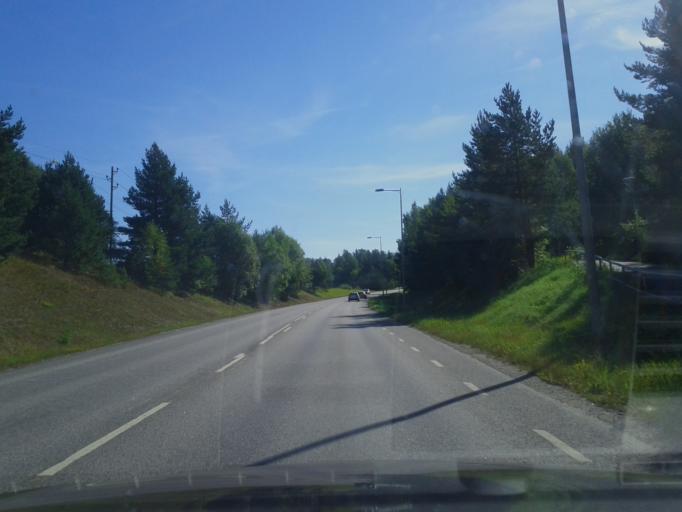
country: SE
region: Stockholm
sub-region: Taby Kommun
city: Taby
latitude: 59.4656
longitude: 18.0635
